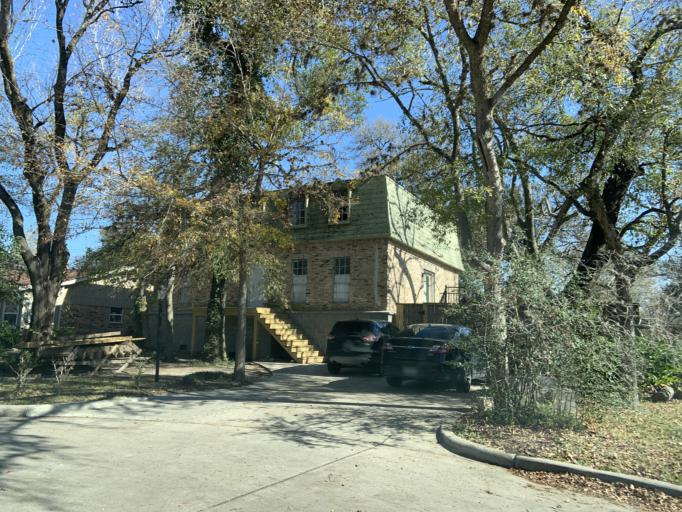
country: US
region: Texas
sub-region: Harris County
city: Bellaire
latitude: 29.6772
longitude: -95.5108
